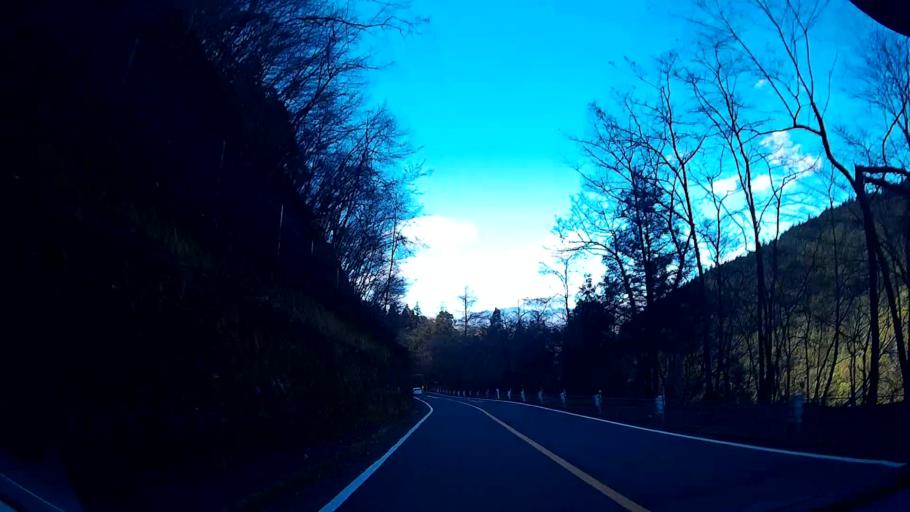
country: JP
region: Yamanashi
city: Uenohara
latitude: 35.7552
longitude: 139.0348
